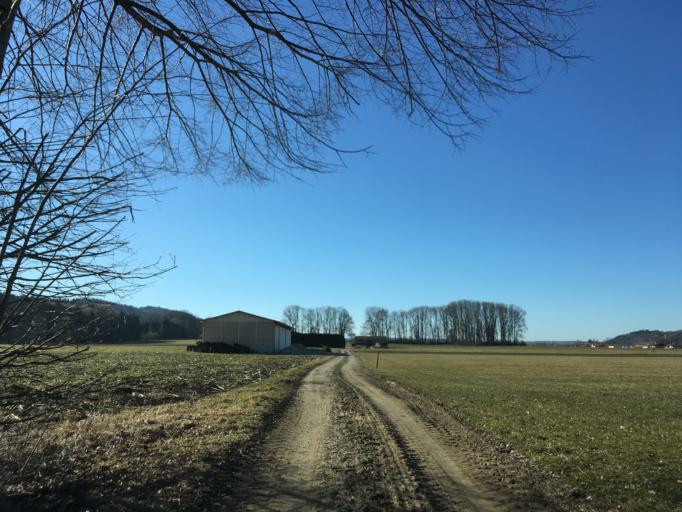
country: DE
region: Bavaria
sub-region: Upper Bavaria
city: Bruckmuhl
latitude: 47.8635
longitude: 11.9186
